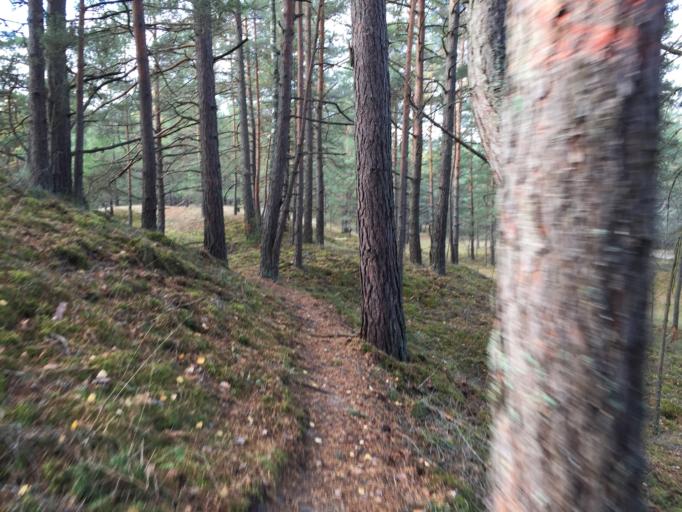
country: LV
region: Carnikava
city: Carnikava
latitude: 57.1490
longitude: 24.2614
